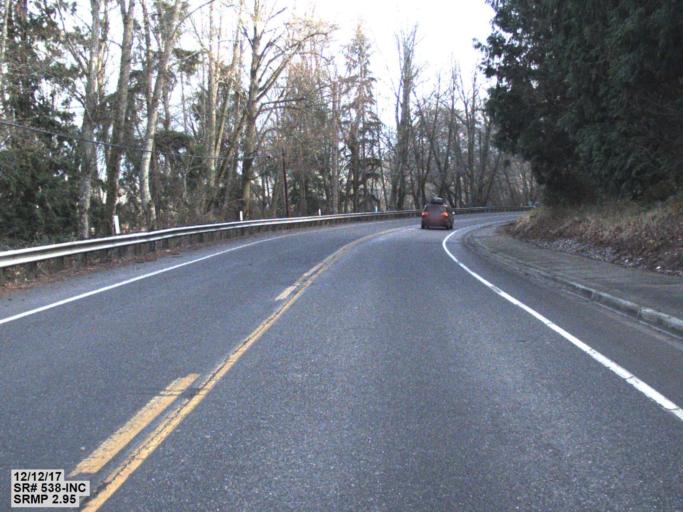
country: US
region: Washington
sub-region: Skagit County
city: Big Lake
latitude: 48.4343
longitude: -122.2772
